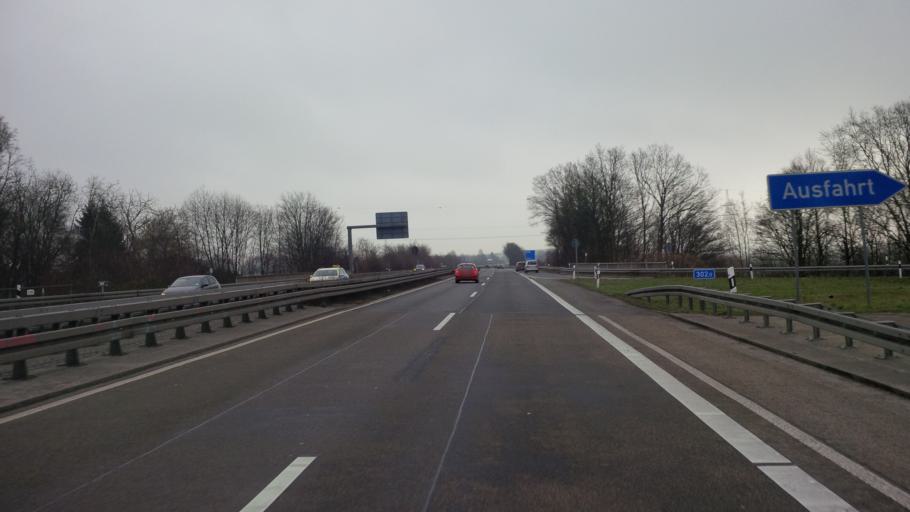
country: DE
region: Hesse
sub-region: Regierungsbezirk Darmstadt
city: Bad Homburg vor der Hoehe
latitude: 50.2106
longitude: 8.6038
